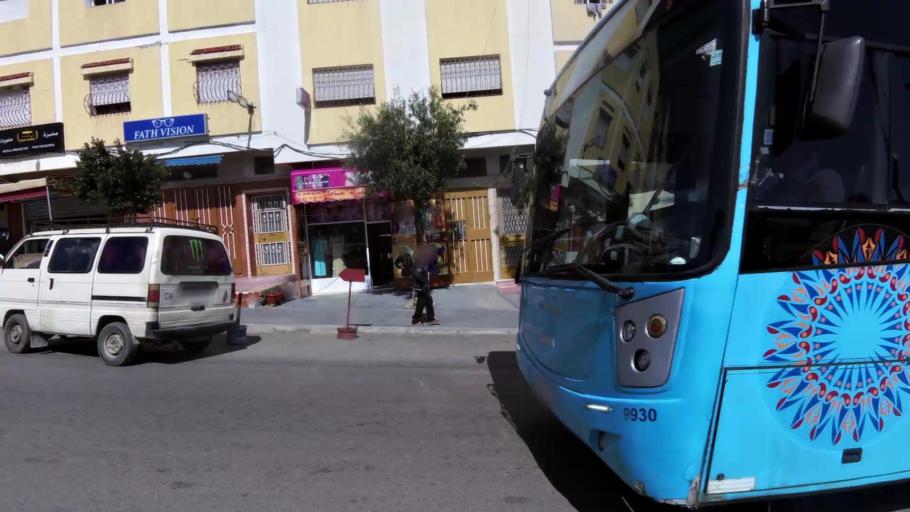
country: MA
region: Tanger-Tetouan
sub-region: Tanger-Assilah
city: Tangier
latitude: 35.7412
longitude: -5.8123
